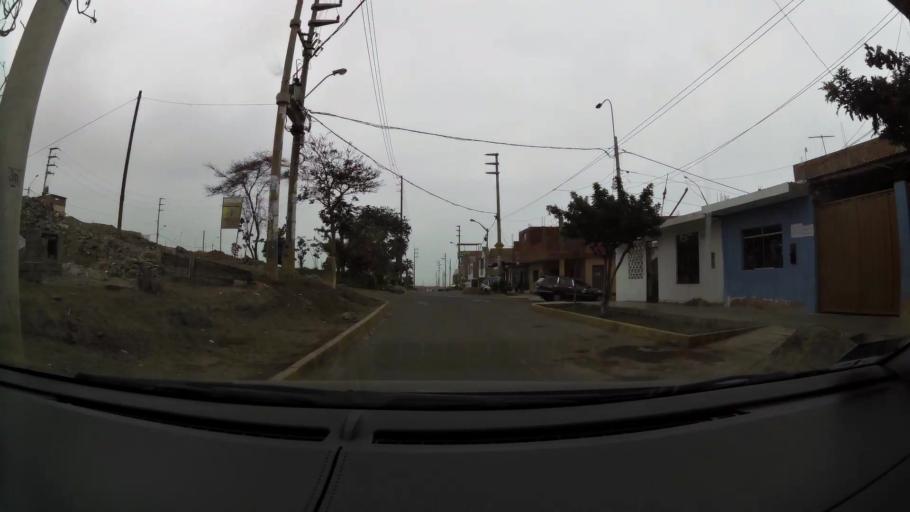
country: PE
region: Lima
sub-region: Provincia de Huaral
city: Chancay
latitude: -11.5922
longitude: -77.2573
